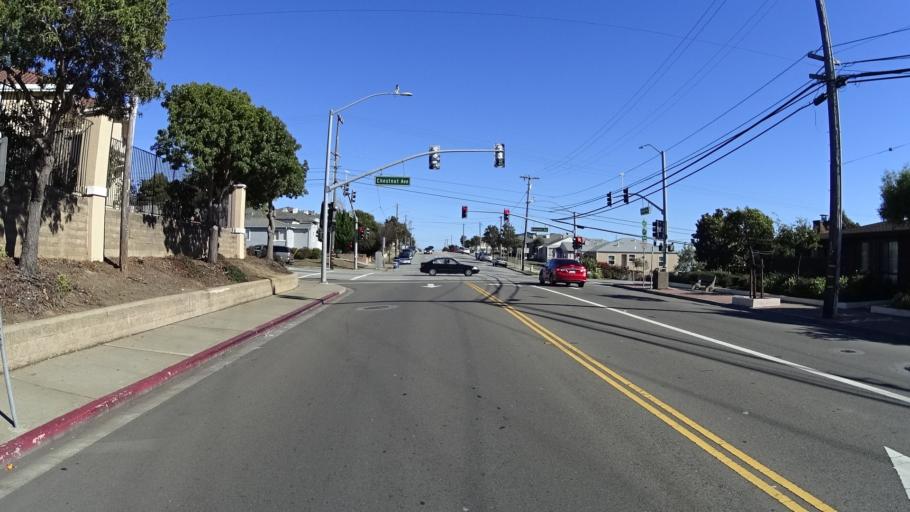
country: US
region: California
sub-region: San Mateo County
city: South San Francisco
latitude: 37.6597
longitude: -122.4306
